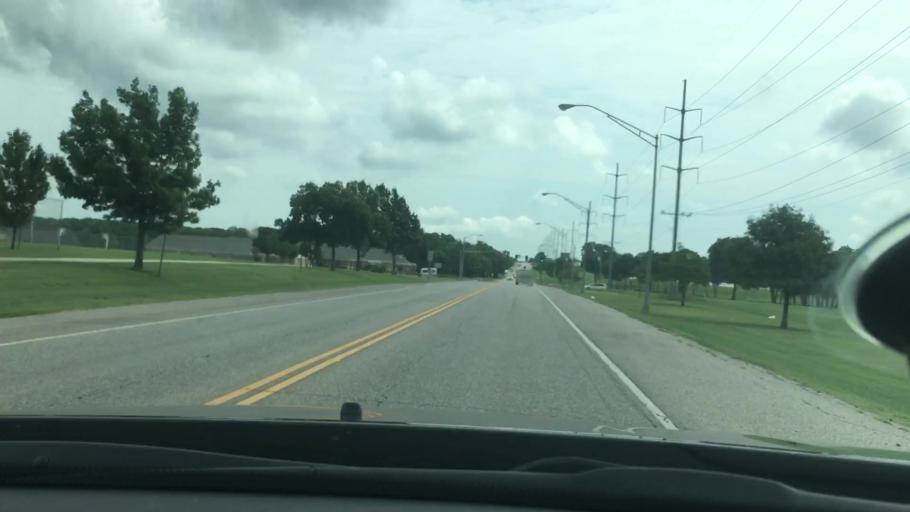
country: US
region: Oklahoma
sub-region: Carter County
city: Ardmore
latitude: 34.2028
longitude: -97.1278
